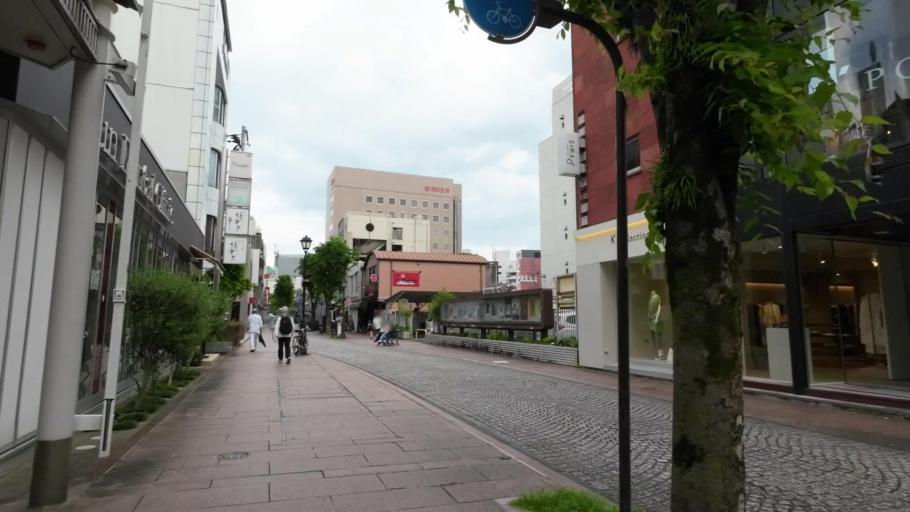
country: JP
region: Kochi
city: Kochi-shi
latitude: 33.5599
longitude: 133.5381
